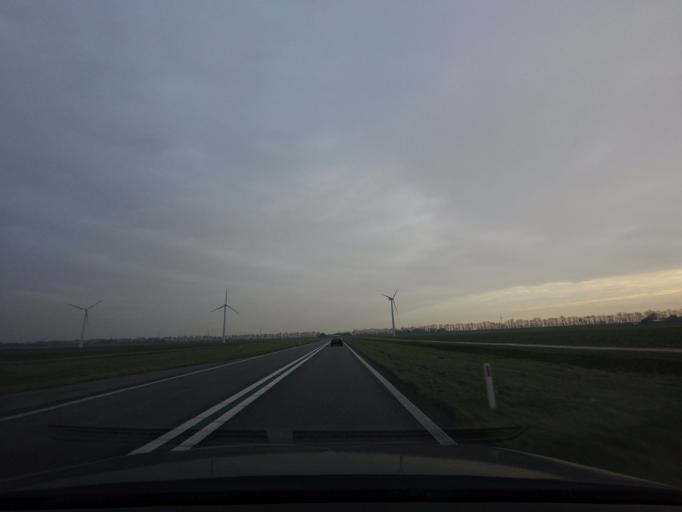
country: NL
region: North Holland
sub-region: Gemeente Opmeer
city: Opmeer
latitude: 52.7591
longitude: 4.9368
